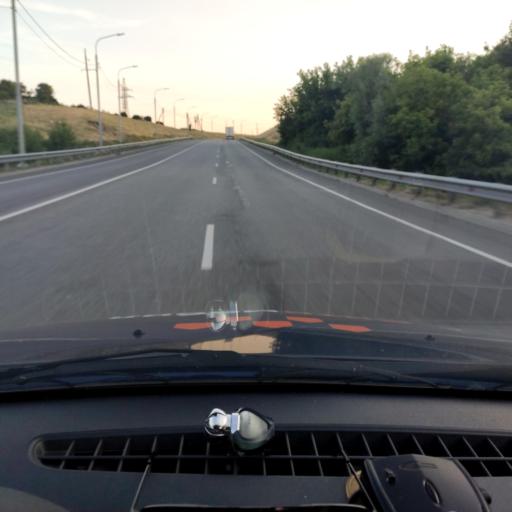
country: RU
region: Voronezj
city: Nizhnedevitsk
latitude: 51.5674
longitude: 38.4695
